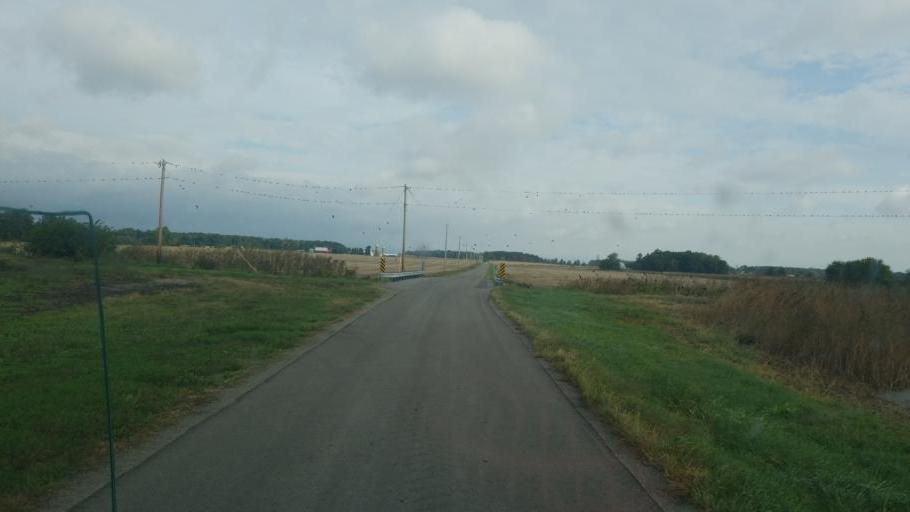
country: US
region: Ohio
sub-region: Wyandot County
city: Carey
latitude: 41.0203
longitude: -83.4488
